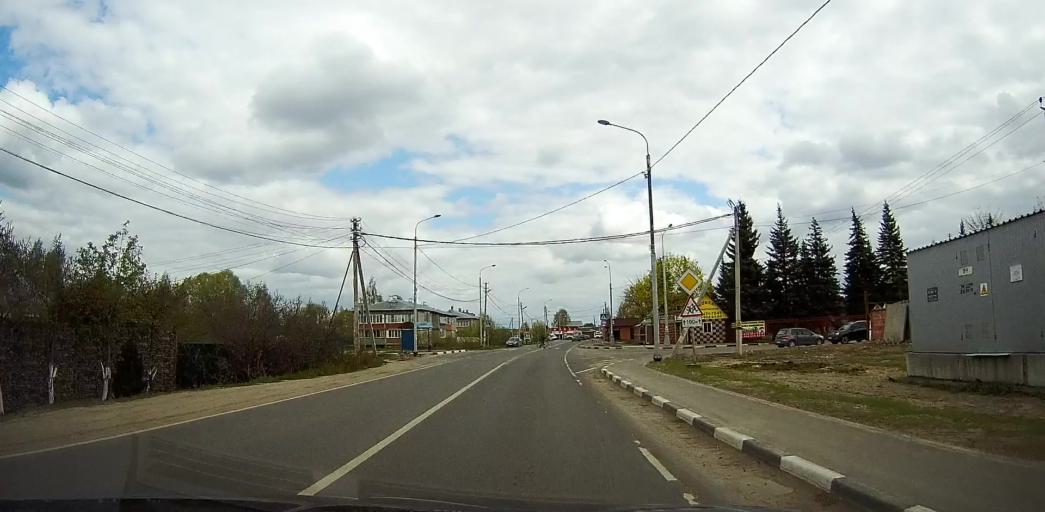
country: RU
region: Moskovskaya
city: Ashitkovo
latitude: 55.4254
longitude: 38.5762
